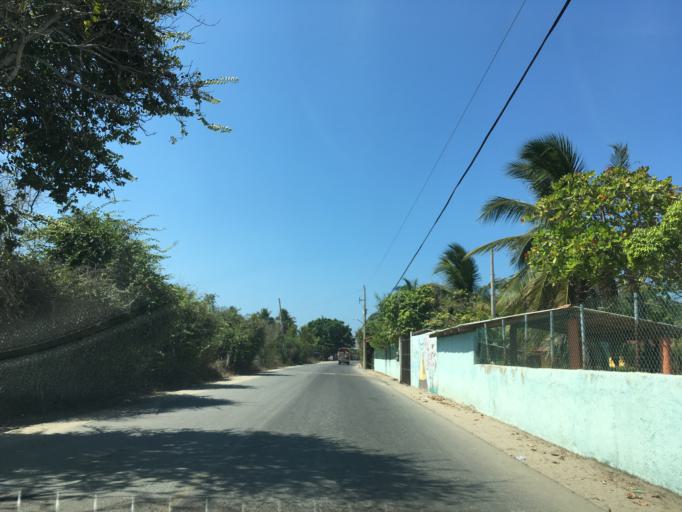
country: MX
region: Guerrero
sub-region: Zihuatanejo de Azueta
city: Los Achotes
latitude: 17.5402
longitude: -101.4404
